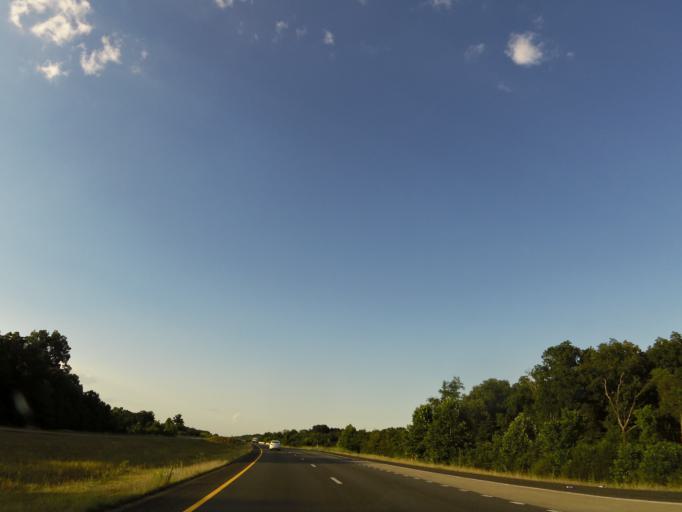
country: US
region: Tennessee
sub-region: Rutherford County
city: Murfreesboro
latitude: 35.9086
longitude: -86.4434
